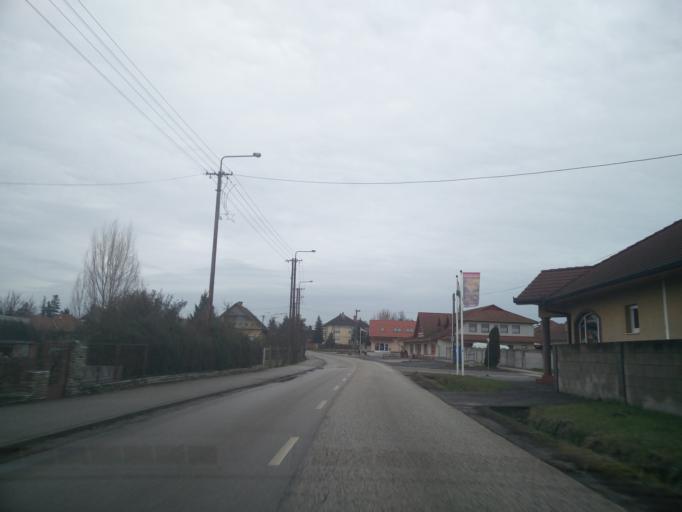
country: HU
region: Pest
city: Koka
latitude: 47.4856
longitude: 19.5781
